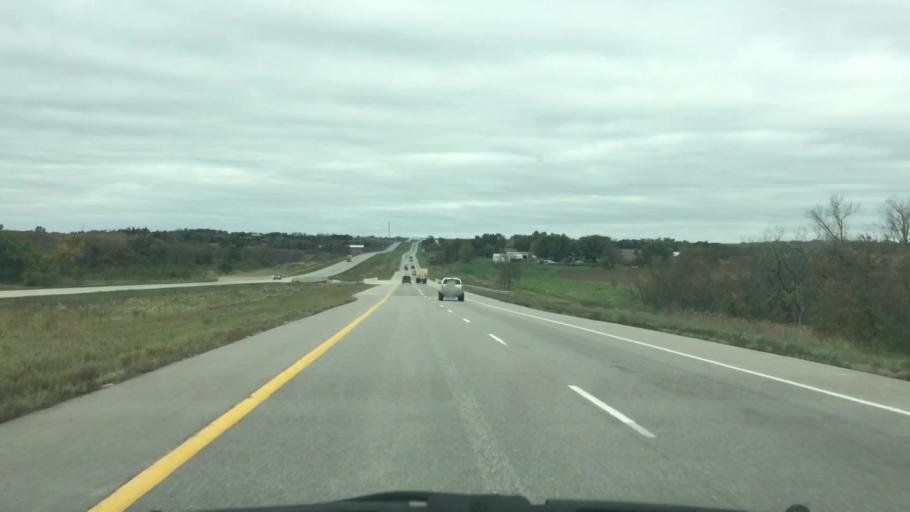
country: US
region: Iowa
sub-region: Warren County
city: Norwalk
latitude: 41.4533
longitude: -93.7795
